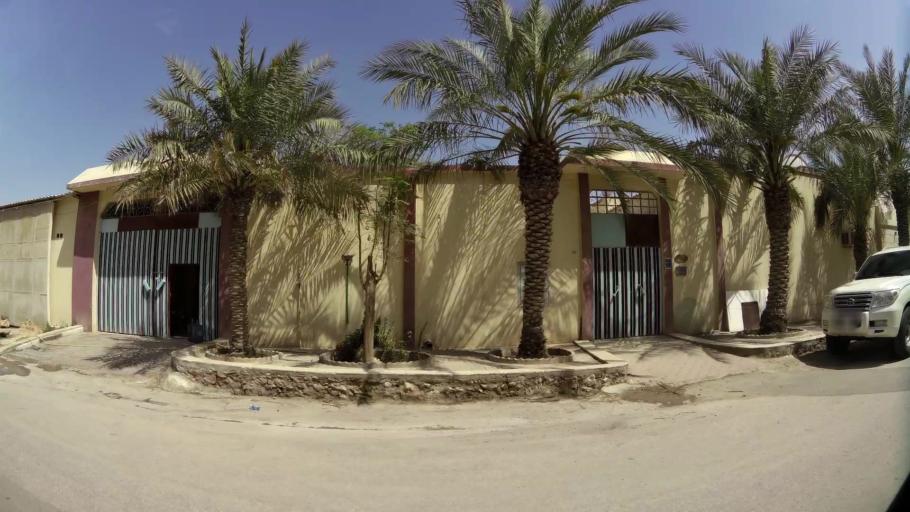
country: QA
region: Baladiyat Umm Salal
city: Umm Salal Muhammad
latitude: 25.3693
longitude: 51.4264
